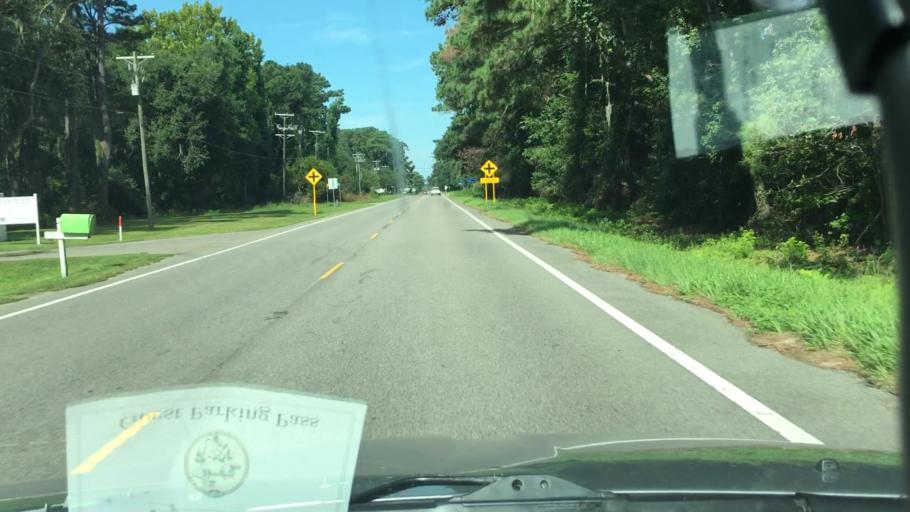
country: US
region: South Carolina
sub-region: Beaufort County
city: Beaufort
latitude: 32.4148
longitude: -80.4925
